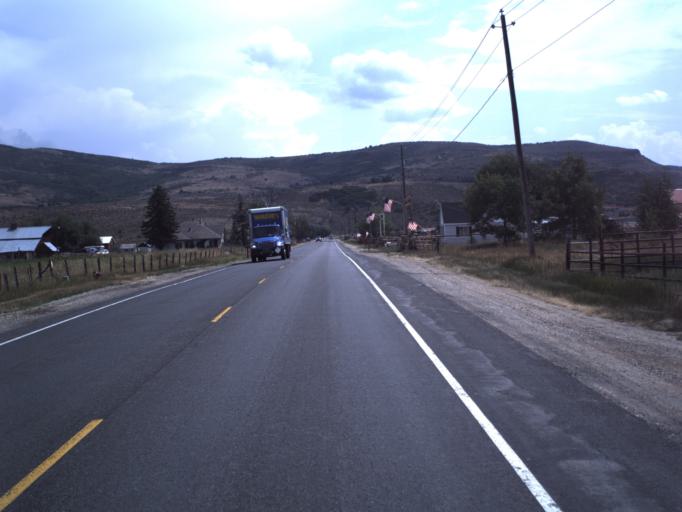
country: US
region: Utah
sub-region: Summit County
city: Francis
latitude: 40.6105
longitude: -111.2692
